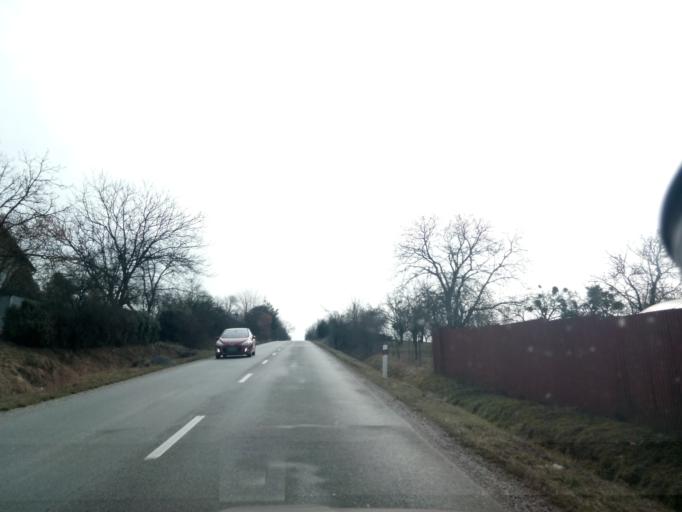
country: SK
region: Kosicky
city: Secovce
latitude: 48.6279
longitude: 21.5265
